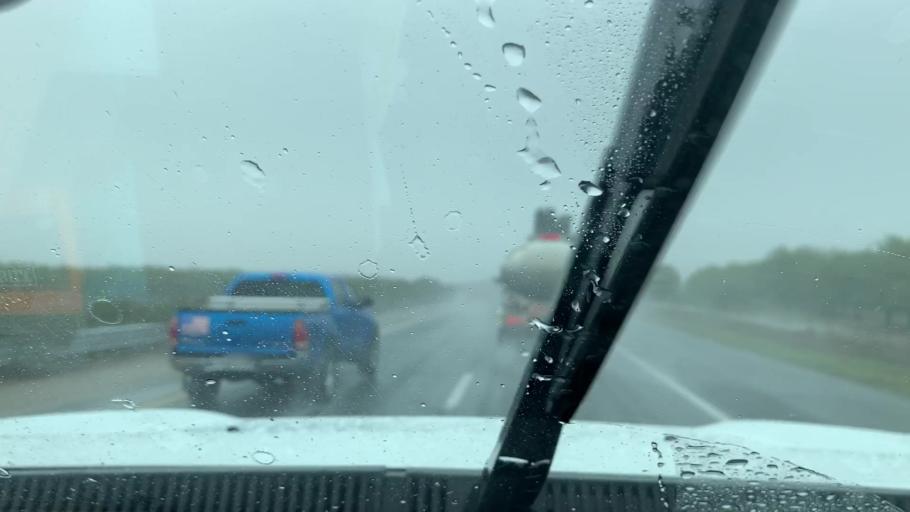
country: US
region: California
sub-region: Tulare County
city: Earlimart
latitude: 35.8442
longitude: -119.2648
